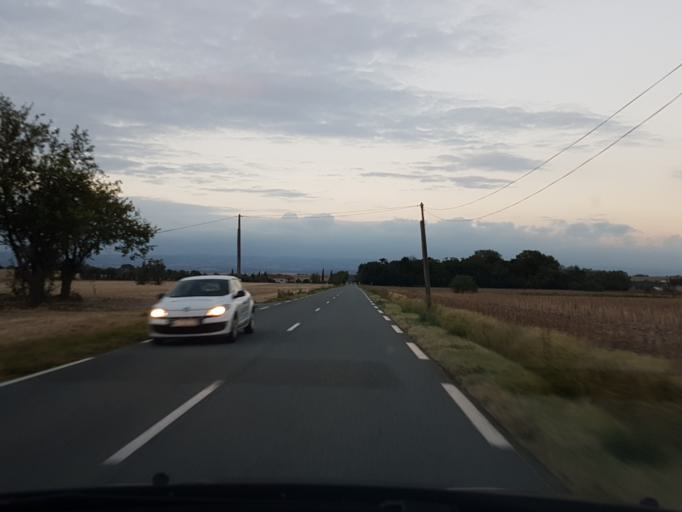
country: FR
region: Languedoc-Roussillon
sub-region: Departement de l'Aude
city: Bram
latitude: 43.2063
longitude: 2.0642
